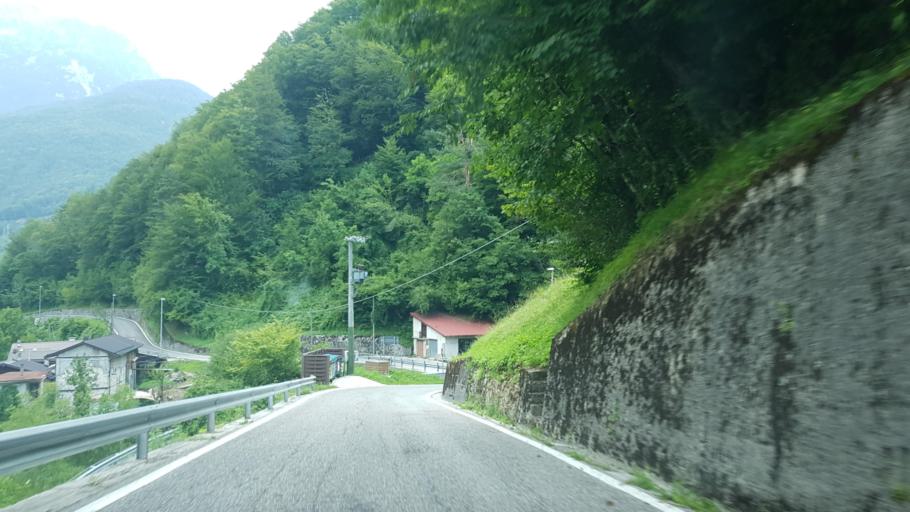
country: IT
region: Friuli Venezia Giulia
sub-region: Provincia di Udine
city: Dogna
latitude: 46.4493
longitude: 13.3291
